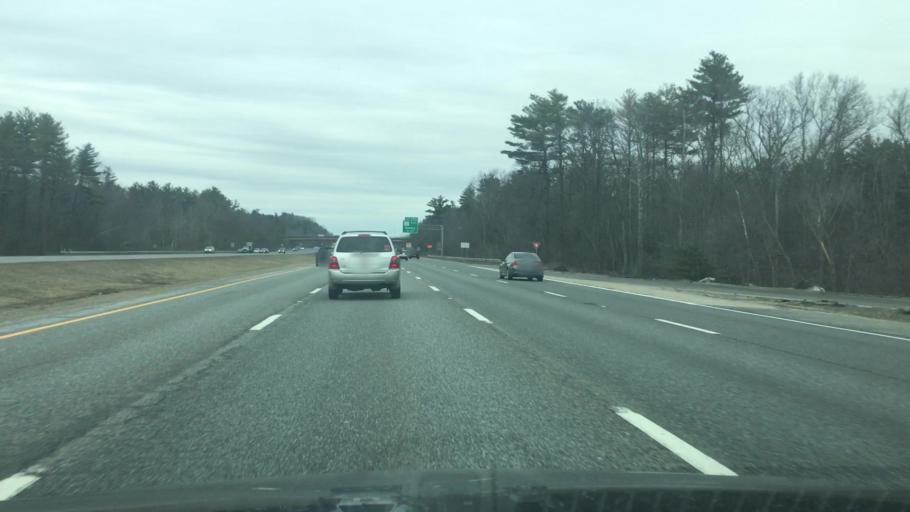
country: US
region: Massachusetts
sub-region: Essex County
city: Boxford
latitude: 42.6978
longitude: -70.9685
